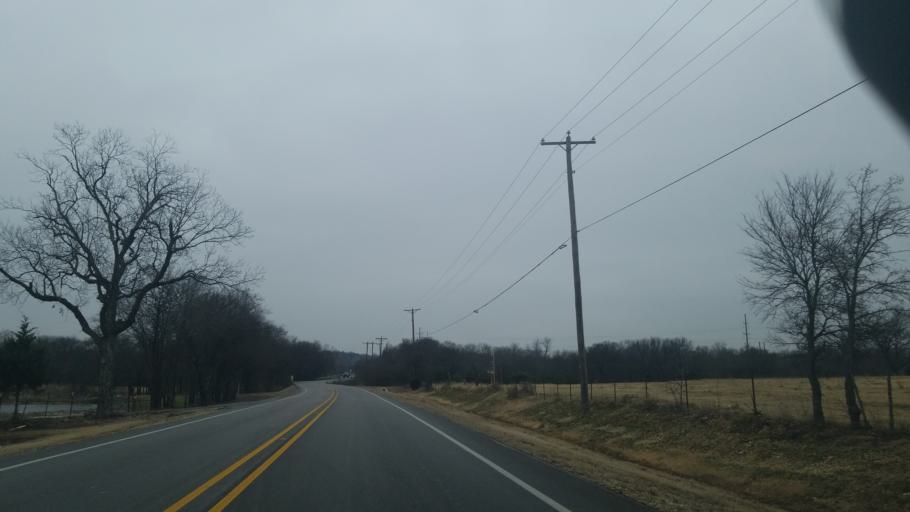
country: US
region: Texas
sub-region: Denton County
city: Argyle
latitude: 33.1548
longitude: -97.1420
